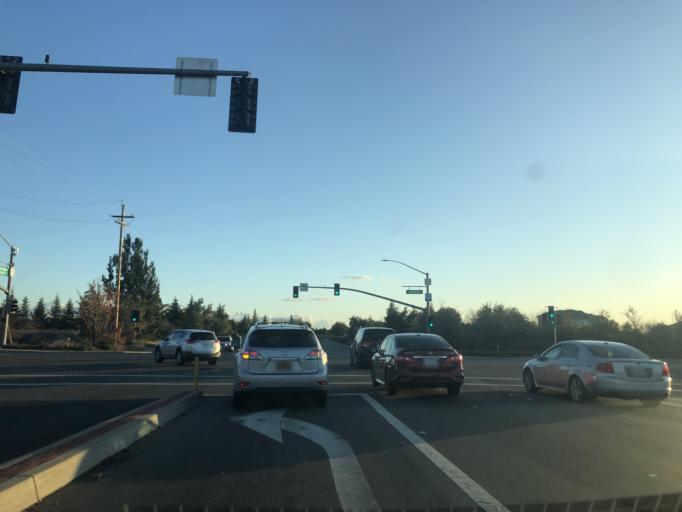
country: US
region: California
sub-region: Sacramento County
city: Antelope
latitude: 38.7522
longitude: -121.3586
